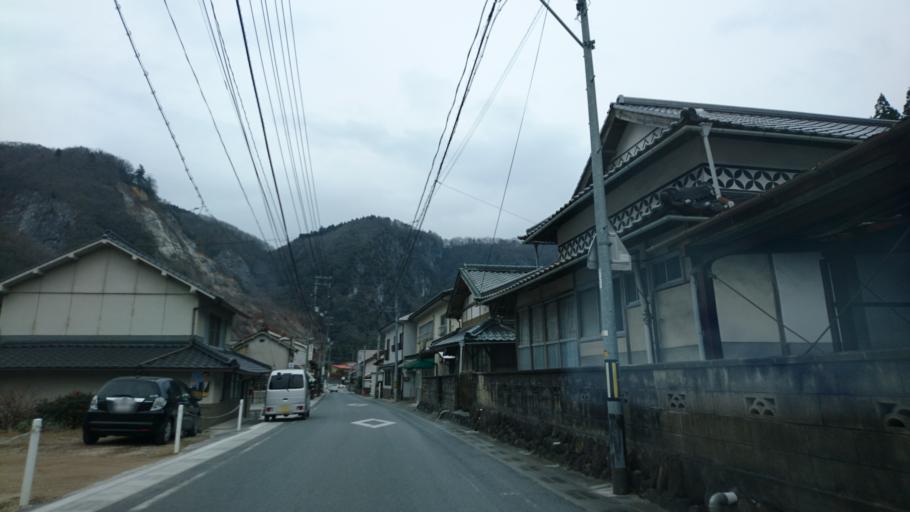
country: JP
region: Okayama
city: Niimi
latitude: 34.9312
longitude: 133.5165
